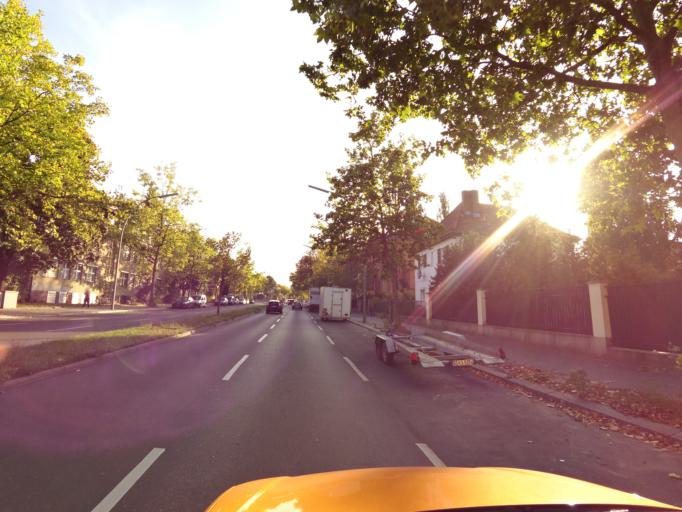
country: DE
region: Berlin
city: Wilmersdorf Bezirk
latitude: 52.4901
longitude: 13.3083
